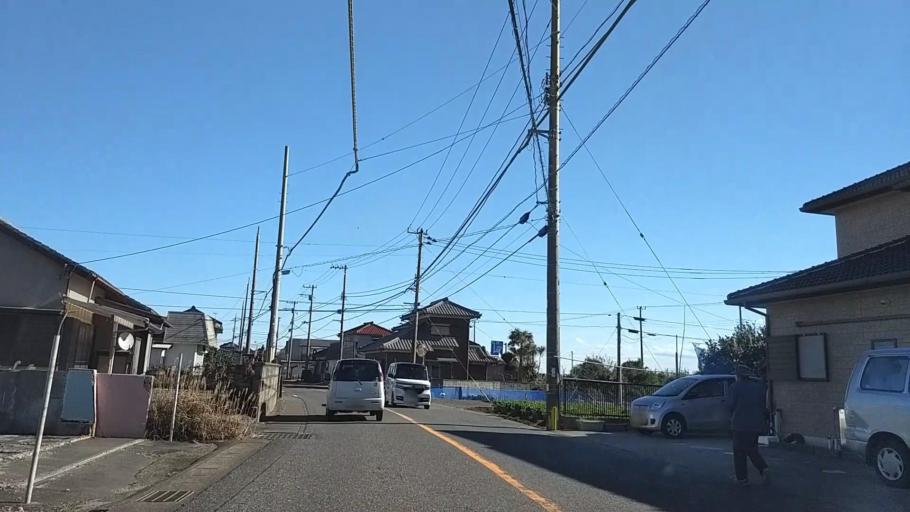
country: JP
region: Chiba
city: Tateyama
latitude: 34.9083
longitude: 139.9076
